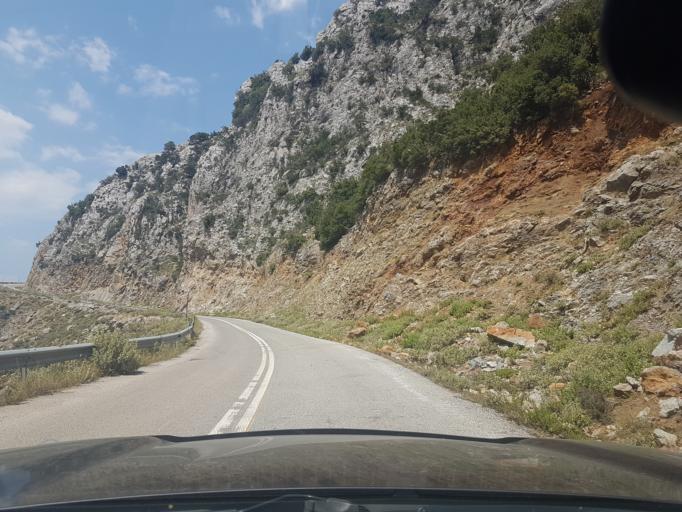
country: GR
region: Central Greece
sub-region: Nomos Evvoias
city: Kymi
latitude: 38.6532
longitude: 23.9678
